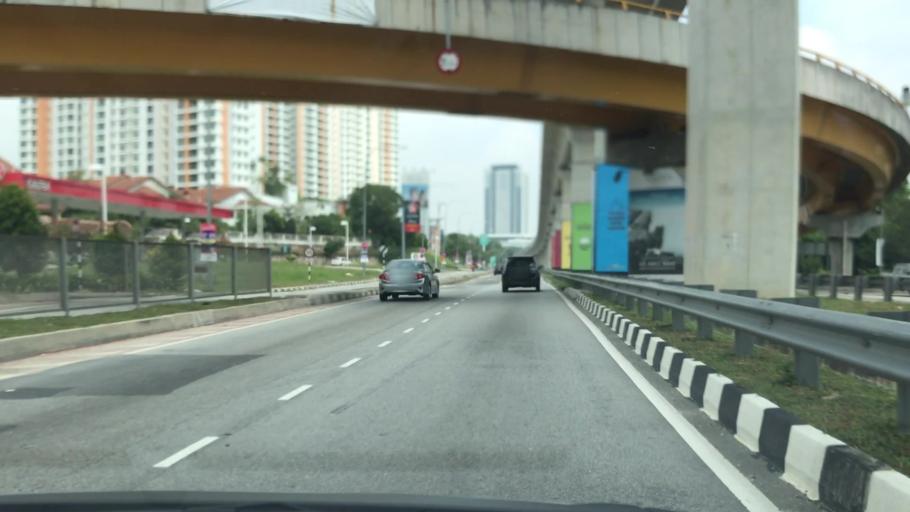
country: MY
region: Selangor
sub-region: Petaling
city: Petaling Jaya
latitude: 3.0543
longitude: 101.6558
